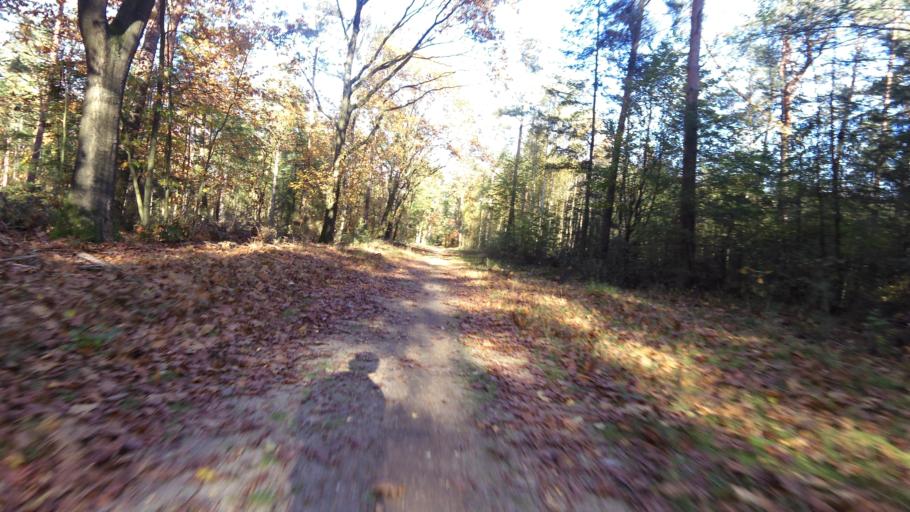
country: NL
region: Gelderland
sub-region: Gemeente Epe
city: Epe
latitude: 52.3655
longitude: 5.9681
